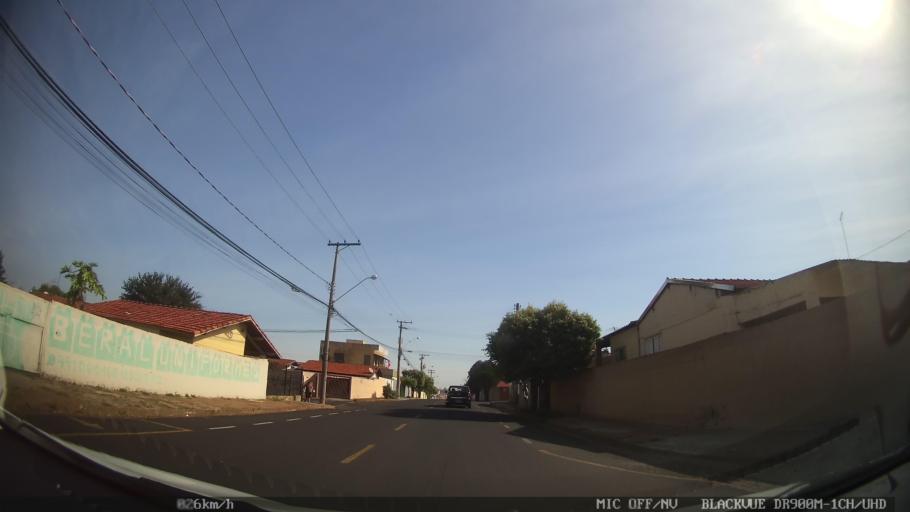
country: BR
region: Sao Paulo
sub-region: Sao Jose Do Rio Preto
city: Sao Jose do Rio Preto
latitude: -20.7962
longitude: -49.4193
